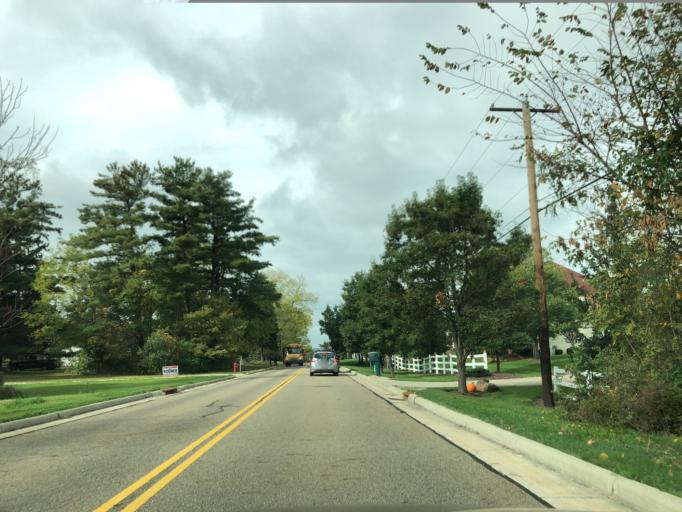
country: US
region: Ohio
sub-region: Summit County
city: Boston Heights
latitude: 41.2633
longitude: -81.5197
